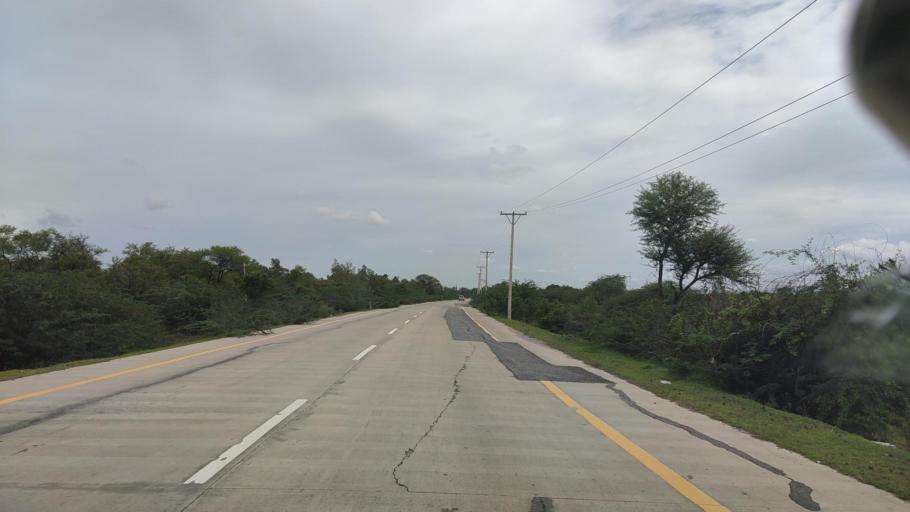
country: MM
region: Mandalay
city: Meiktila
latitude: 21.1340
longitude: 96.0274
